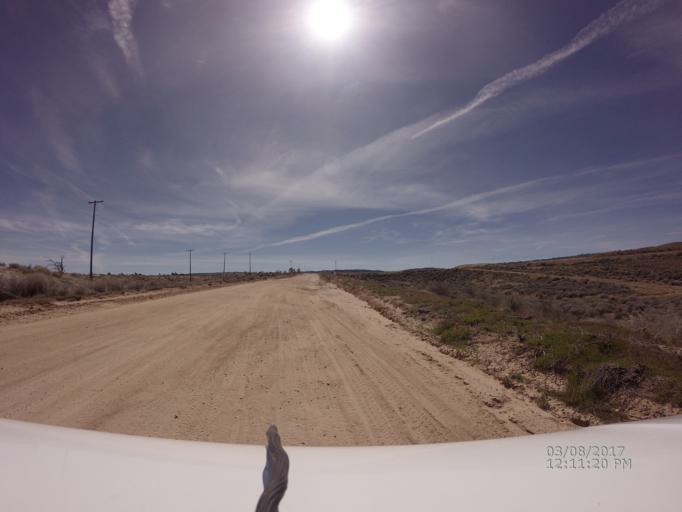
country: US
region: California
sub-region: Los Angeles County
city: Green Valley
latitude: 34.7229
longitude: -118.4300
